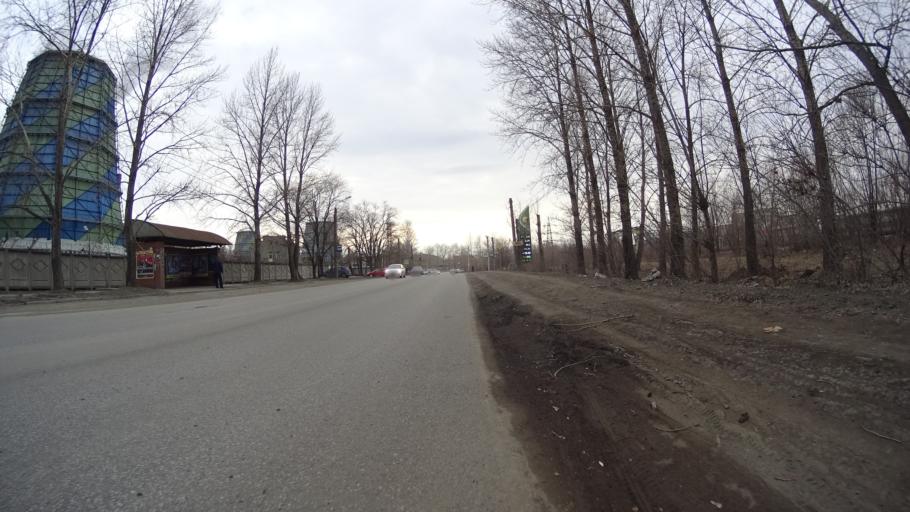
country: RU
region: Chelyabinsk
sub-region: Gorod Chelyabinsk
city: Chelyabinsk
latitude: 55.1563
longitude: 61.5001
